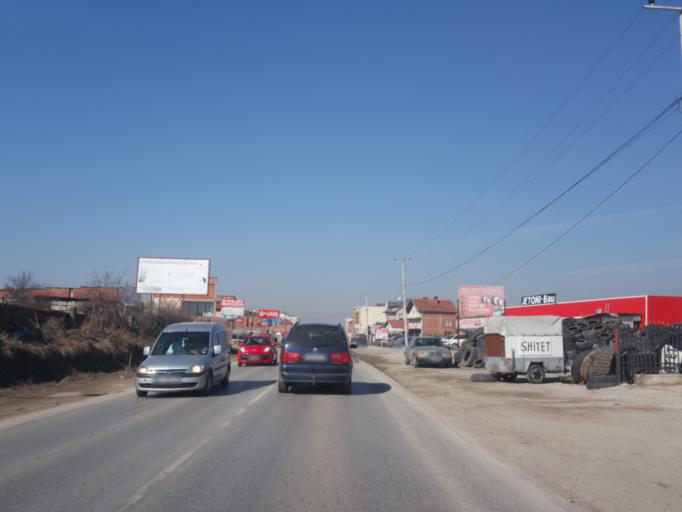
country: XK
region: Mitrovica
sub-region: Vushtrri
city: Vushtrri
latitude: 42.8235
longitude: 20.9758
